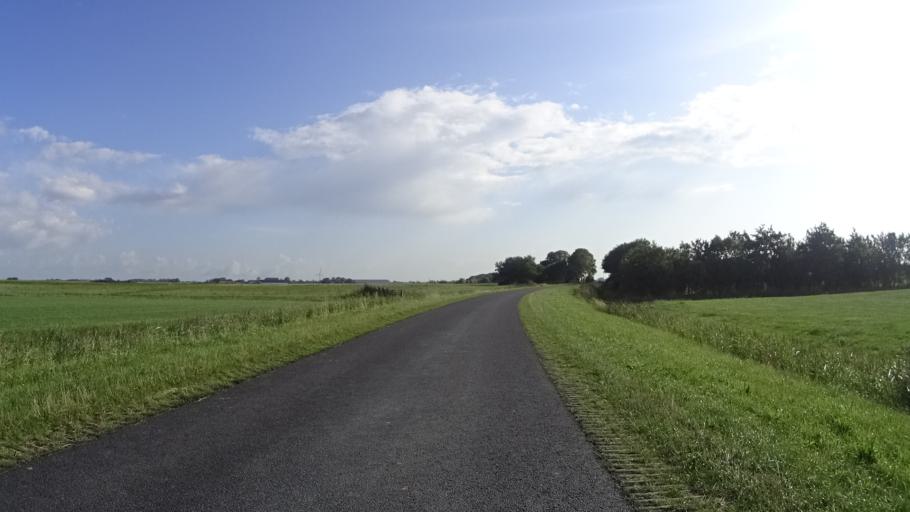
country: NL
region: Friesland
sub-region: Gemeente Harlingen
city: Harlingen
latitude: 53.1179
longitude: 5.4178
